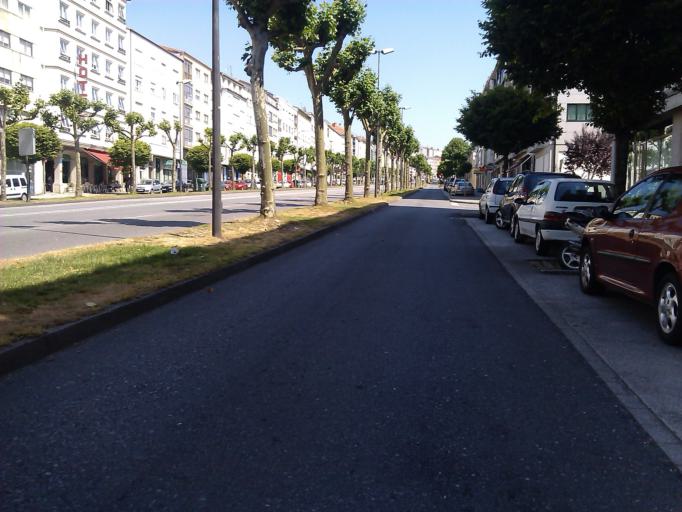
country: ES
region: Galicia
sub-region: Provincia da Coruna
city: Santiago de Compostela
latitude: 42.8805
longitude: -8.5328
